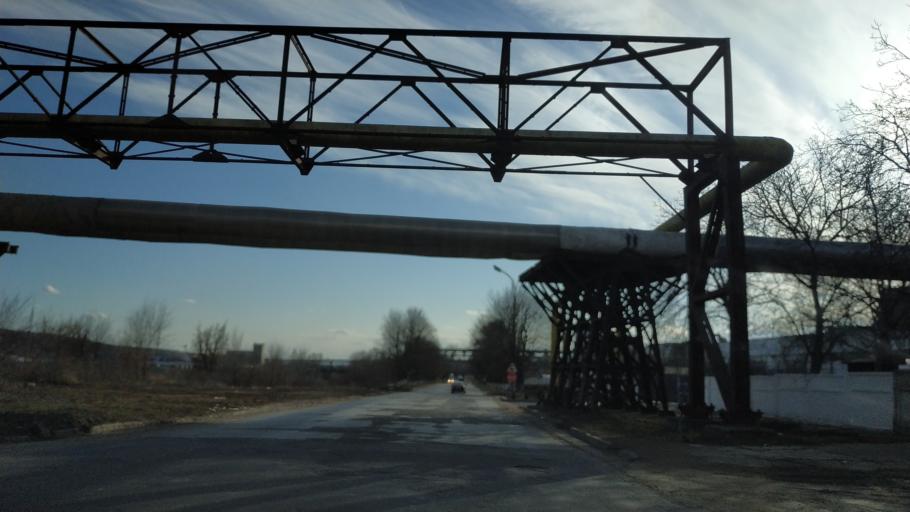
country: MD
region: Chisinau
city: Chisinau
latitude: 47.0309
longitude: 28.8966
